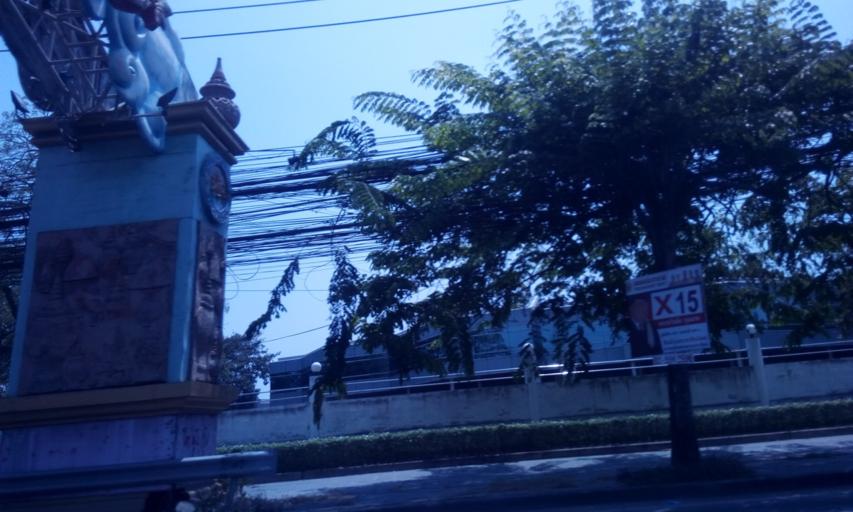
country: TH
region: Nonthaburi
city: Pak Kret
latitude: 13.9068
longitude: 100.5108
